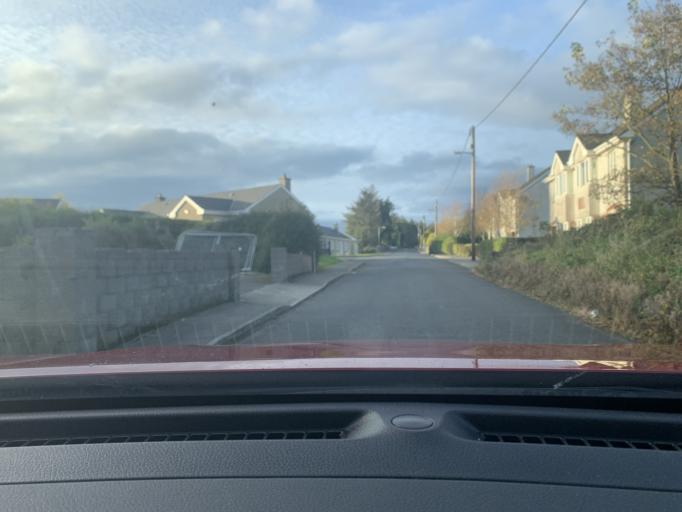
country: IE
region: Connaught
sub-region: Roscommon
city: Ballaghaderreen
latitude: 53.9039
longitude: -8.5755
